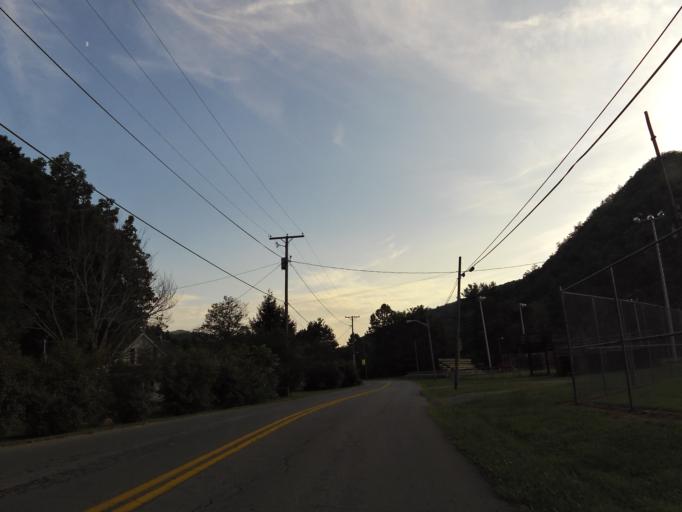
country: US
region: Virginia
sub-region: Washington County
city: Emory
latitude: 36.6298
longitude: -81.7885
